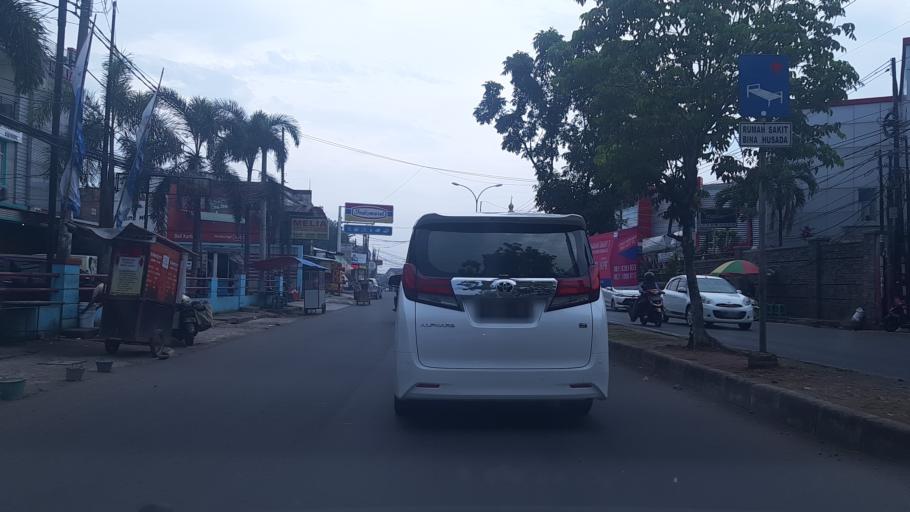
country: ID
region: West Java
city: Cibinong
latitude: -6.4739
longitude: 106.8633
